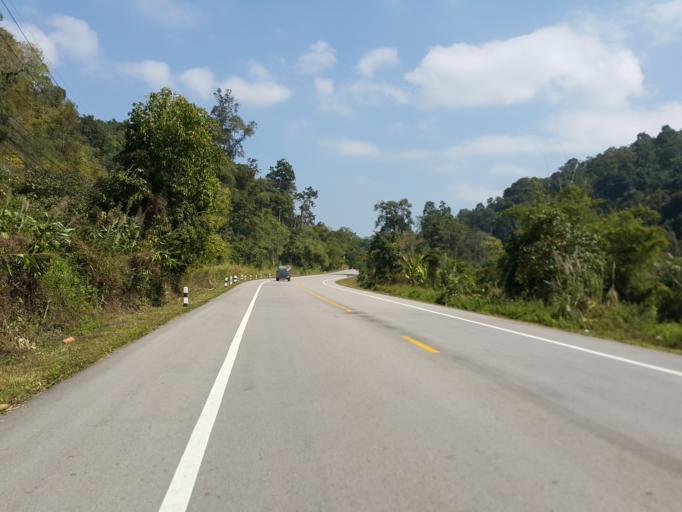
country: TH
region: Chiang Mai
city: Mae On
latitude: 19.0471
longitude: 99.3447
